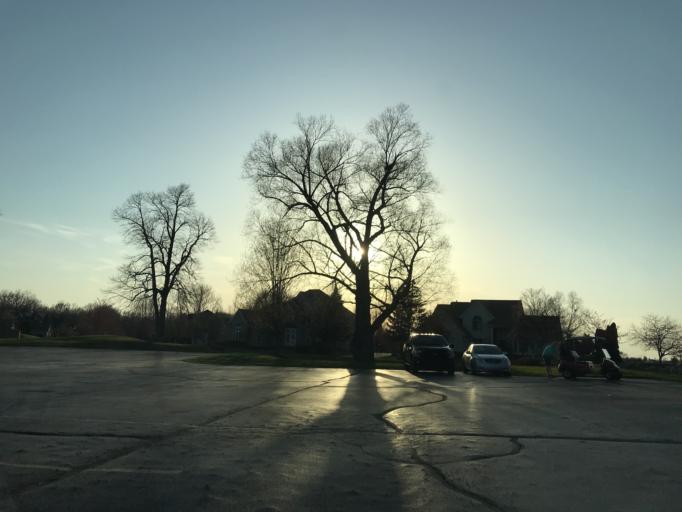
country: US
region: Michigan
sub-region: Oakland County
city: South Lyon
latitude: 42.4558
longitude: -83.5794
